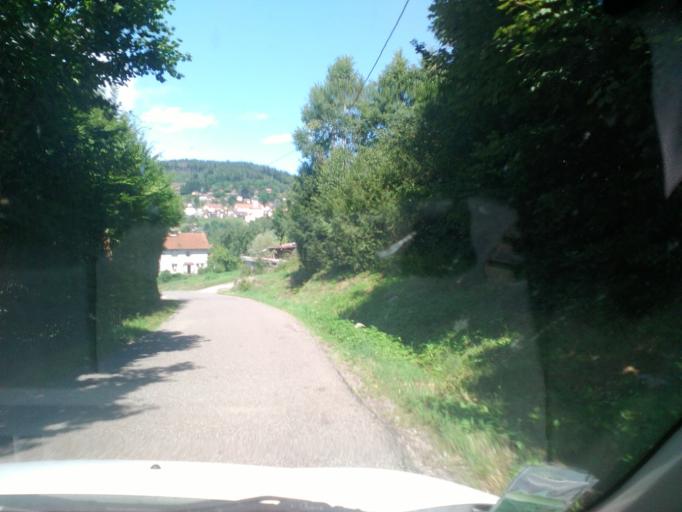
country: FR
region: Lorraine
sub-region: Departement des Vosges
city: Le Tholy
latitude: 48.0733
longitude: 6.7449
